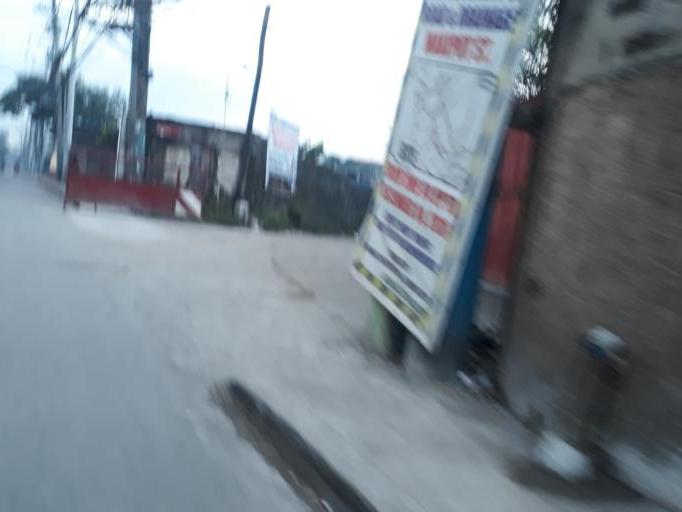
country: PH
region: Calabarzon
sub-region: Province of Rizal
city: Valenzuela
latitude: 14.6952
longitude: 120.9605
